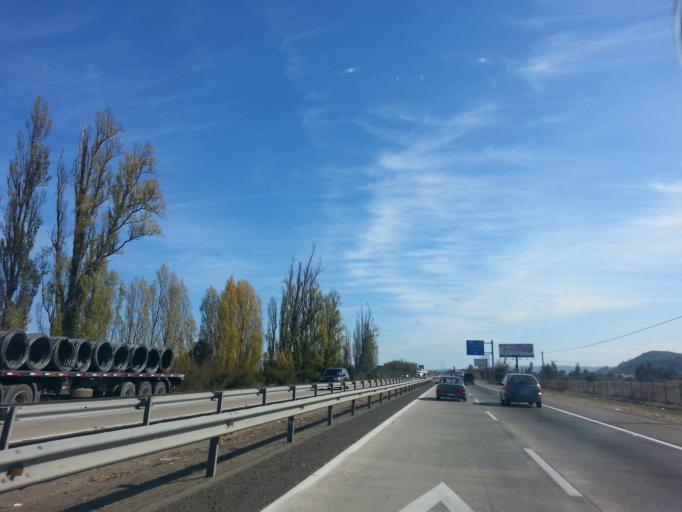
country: CL
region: Valparaiso
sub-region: Provincia de Marga Marga
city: Villa Alemana
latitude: -33.3367
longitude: -71.3748
